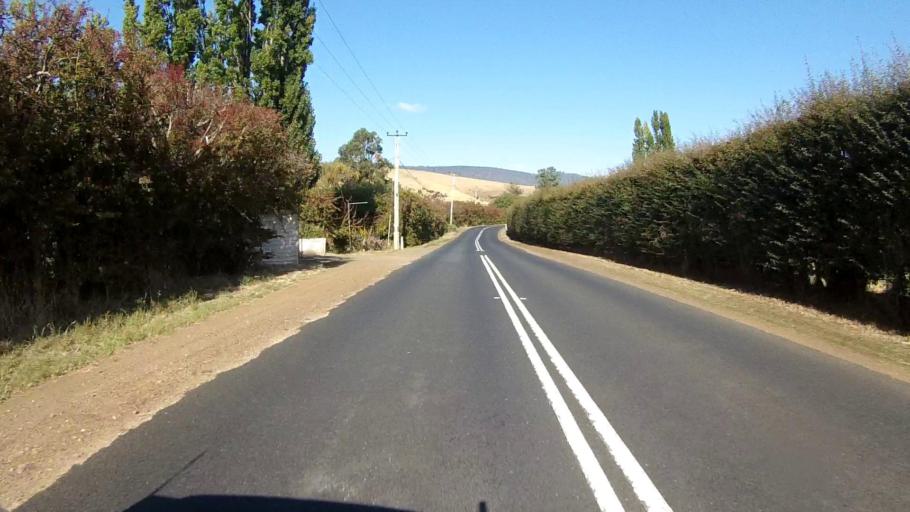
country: AU
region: Tasmania
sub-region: Derwent Valley
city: New Norfolk
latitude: -42.7390
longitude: 146.9554
